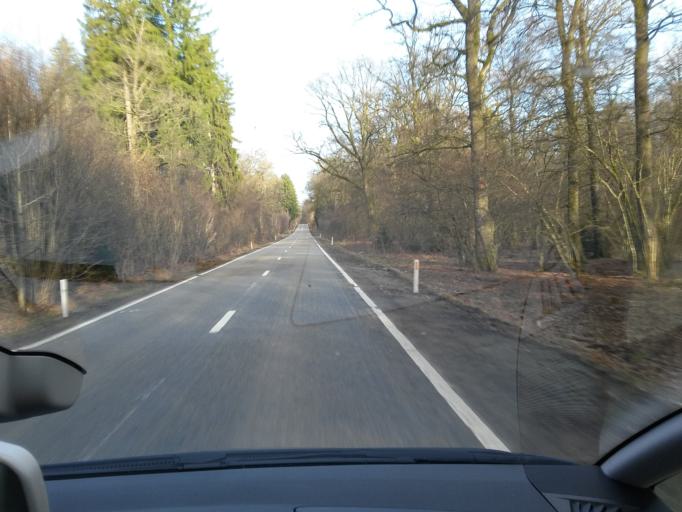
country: BE
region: Wallonia
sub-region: Province du Luxembourg
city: Daverdisse
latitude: 50.0136
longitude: 5.1841
